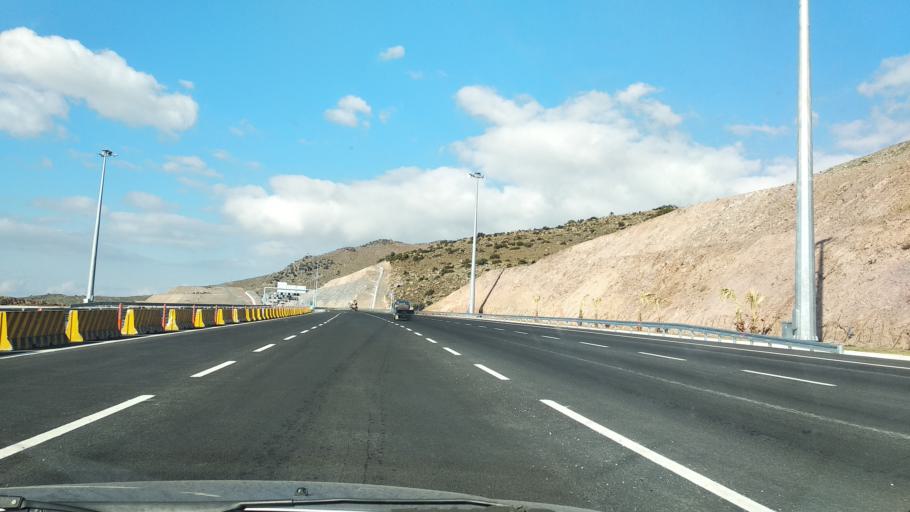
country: TR
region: Izmir
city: Menemen
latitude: 38.6737
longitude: 27.0629
